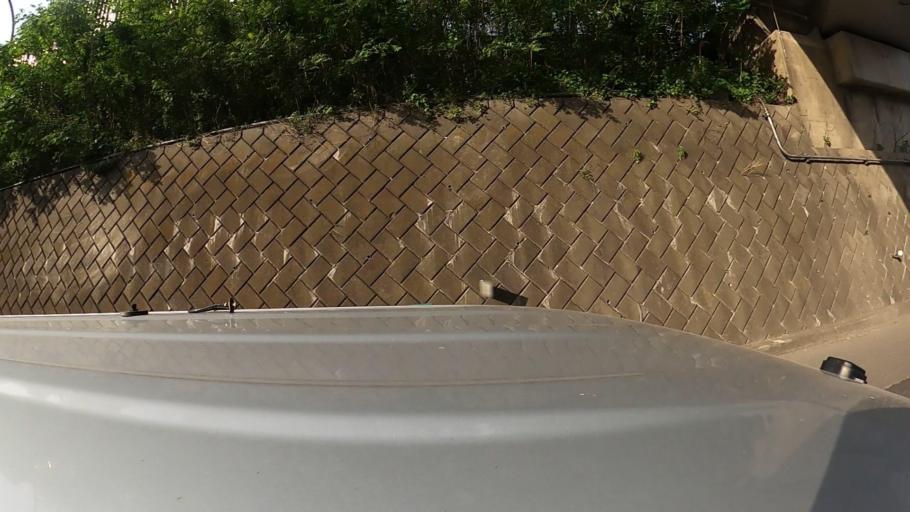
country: JP
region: Saitama
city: Asaka
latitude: 35.7875
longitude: 139.5521
